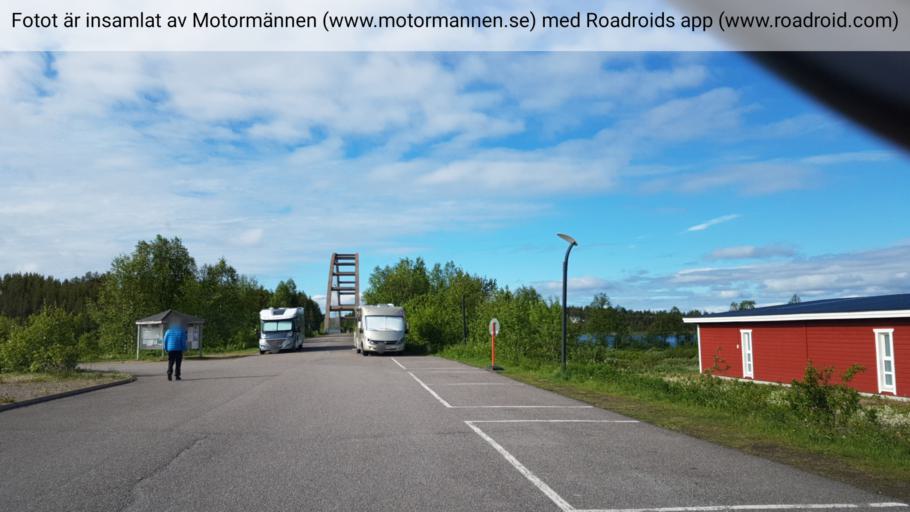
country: SE
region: Norrbotten
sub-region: Gallivare Kommun
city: Malmberget
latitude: 67.4899
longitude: 21.1206
